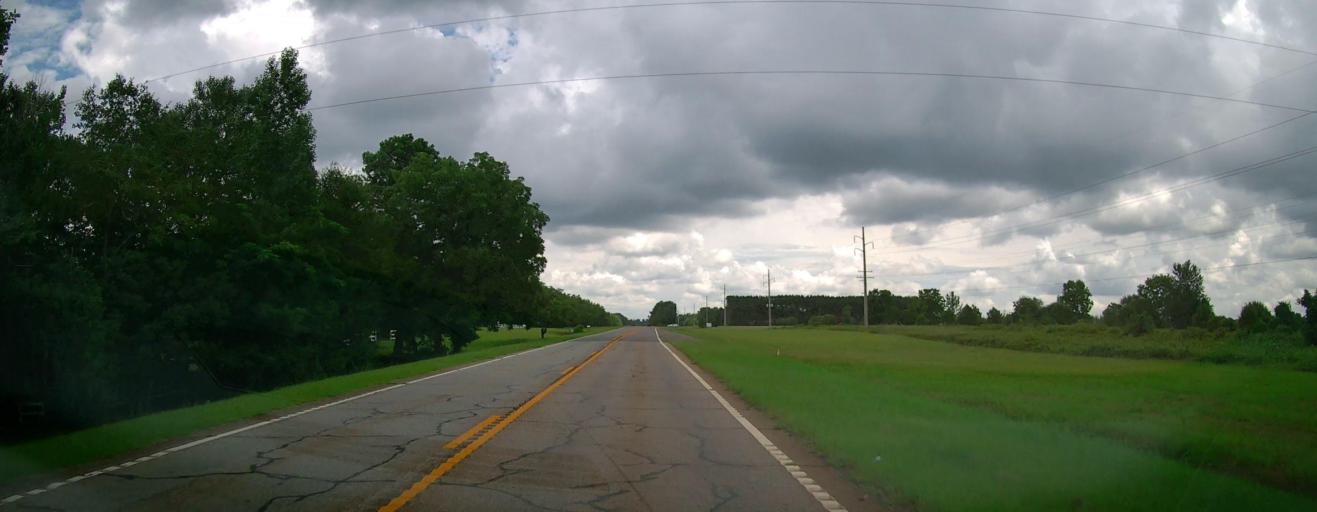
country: US
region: Georgia
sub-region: Pulaski County
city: Hawkinsville
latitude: 32.3208
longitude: -83.5121
